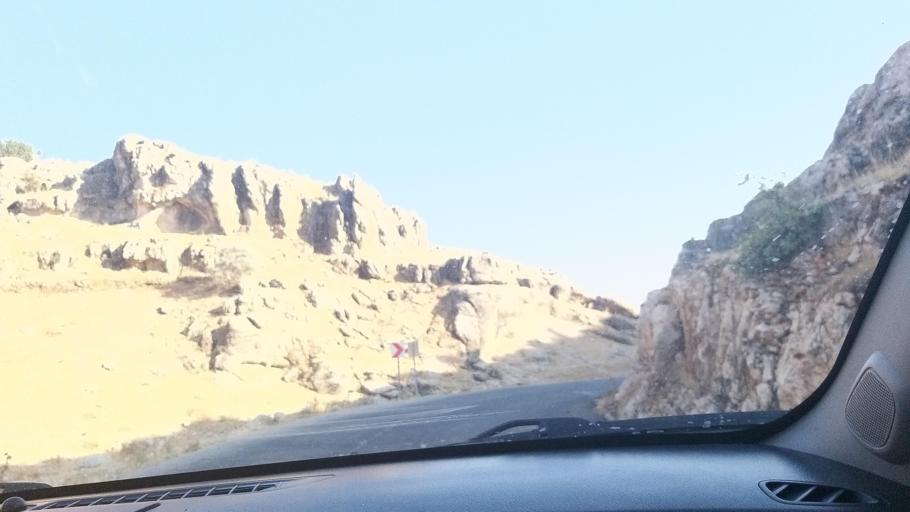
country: TR
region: Diyarbakir
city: Silvan
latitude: 38.1679
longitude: 41.0017
